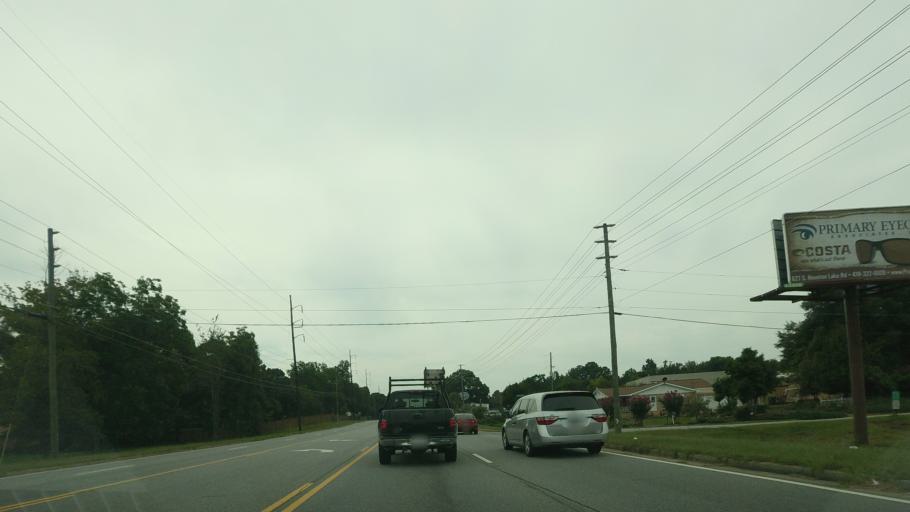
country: US
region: Georgia
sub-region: Houston County
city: Centerville
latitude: 32.5989
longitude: -83.6715
